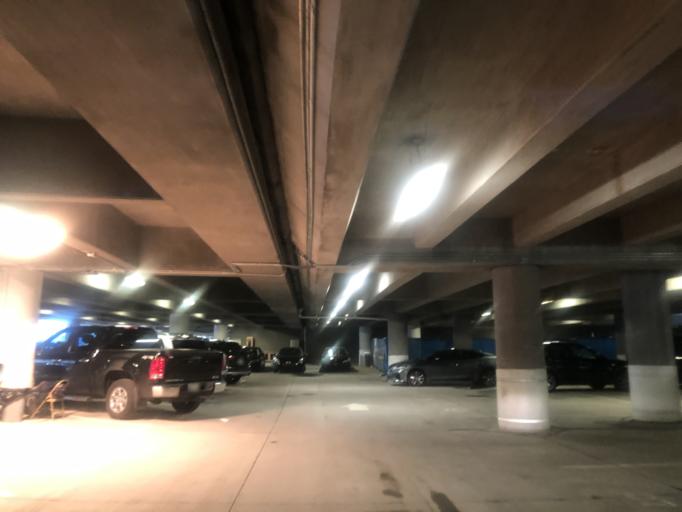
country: US
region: Tennessee
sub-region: Davidson County
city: Lakewood
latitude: 36.1323
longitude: -86.6688
